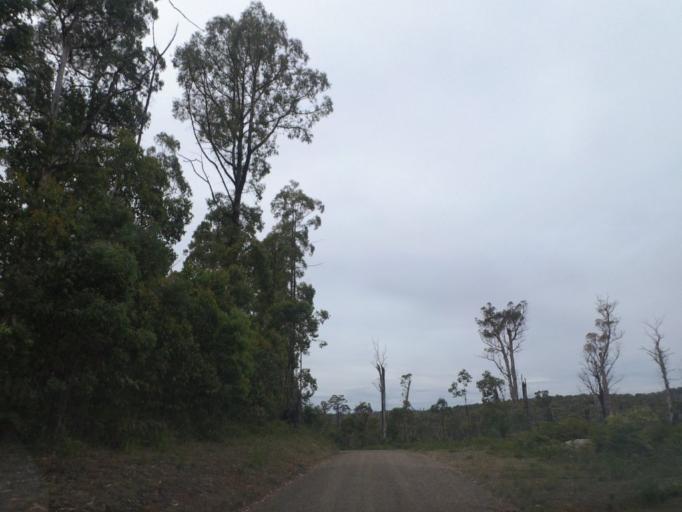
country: AU
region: Victoria
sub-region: Murrindindi
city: Alexandra
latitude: -37.4050
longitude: 145.5925
